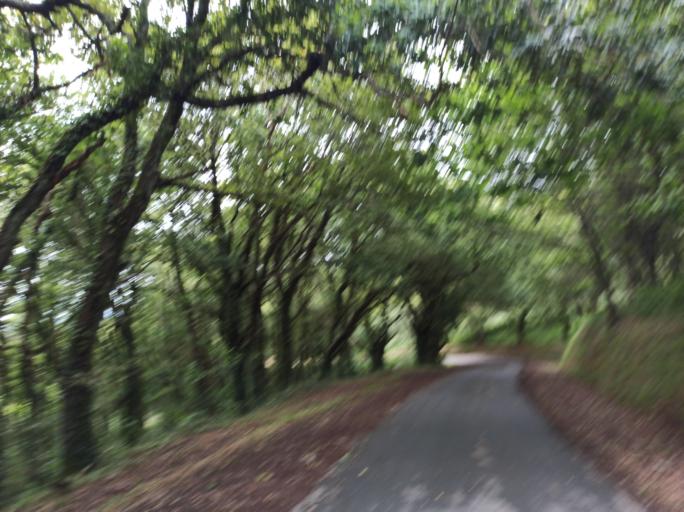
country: ES
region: Galicia
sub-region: Provincia de Pontevedra
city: Silleda
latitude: 42.7702
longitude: -8.1634
